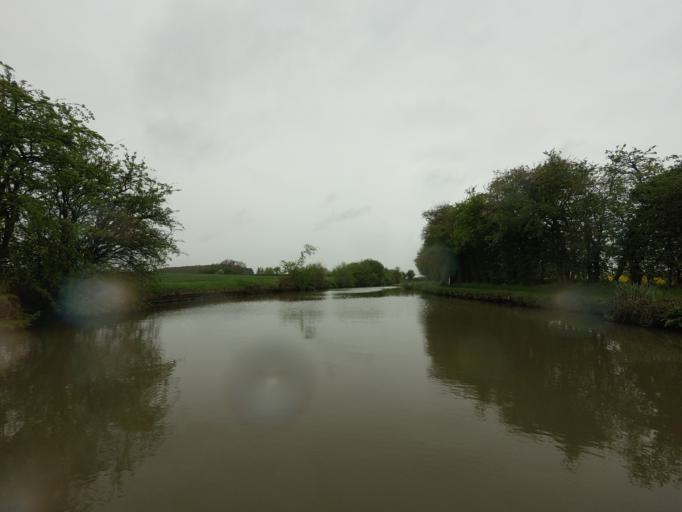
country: GB
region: England
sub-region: Milton Keynes
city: Castlethorpe
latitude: 52.0912
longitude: -0.8607
